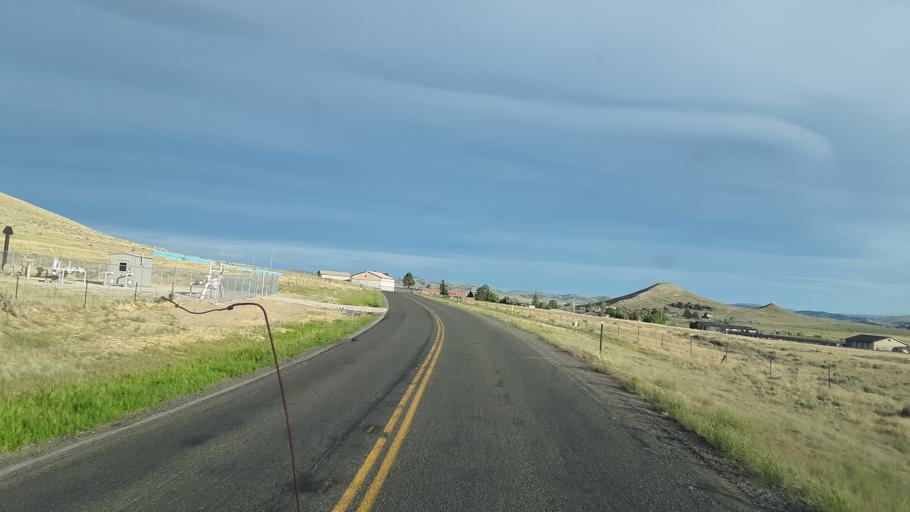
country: US
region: Wyoming
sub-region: Park County
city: Cody
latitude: 44.5165
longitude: -109.0170
